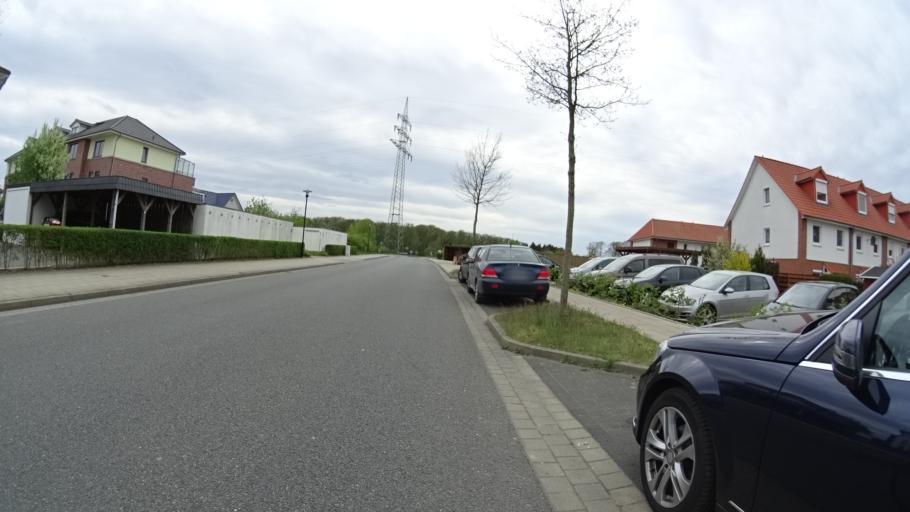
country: DE
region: Lower Saxony
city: Reppenstedt
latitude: 53.2379
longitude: 10.3821
